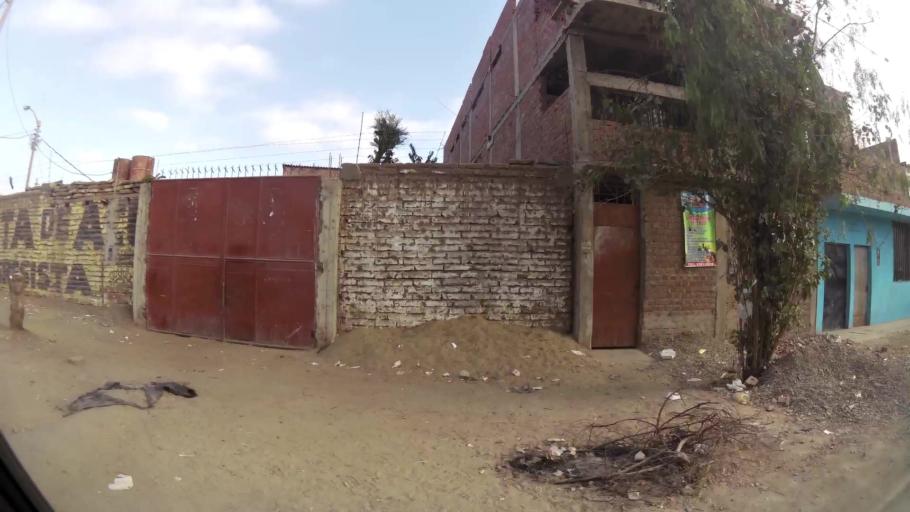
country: PE
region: La Libertad
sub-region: Provincia de Trujillo
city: El Porvenir
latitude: -8.0885
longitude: -79.0211
